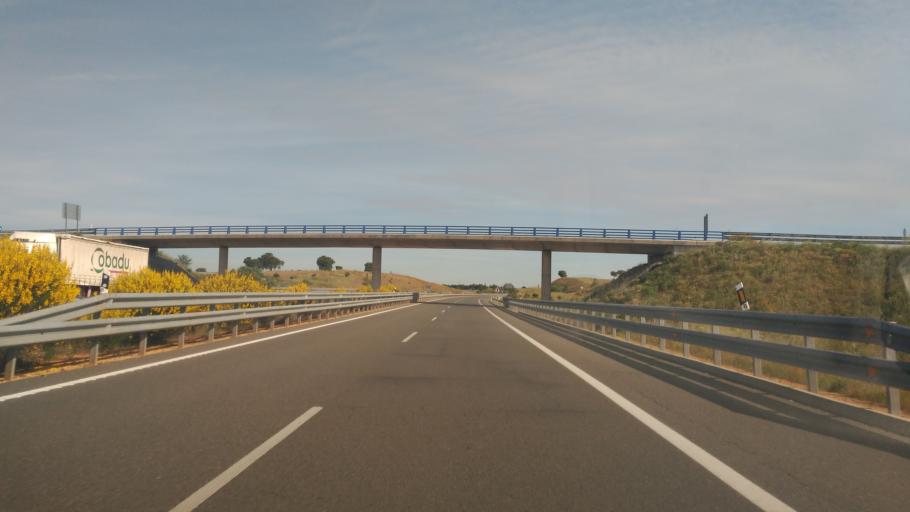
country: ES
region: Castille and Leon
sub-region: Provincia de Zamora
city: Cuelgamures
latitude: 41.2627
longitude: -5.7033
